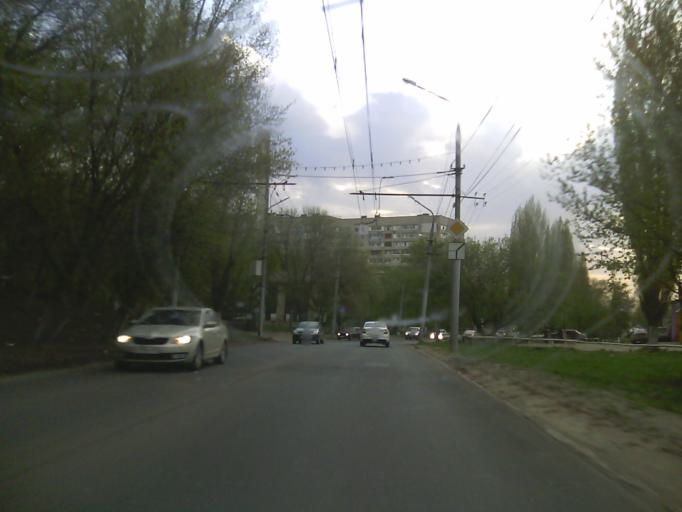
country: RU
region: Saratov
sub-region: Saratovskiy Rayon
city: Saratov
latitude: 51.5920
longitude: 45.9278
